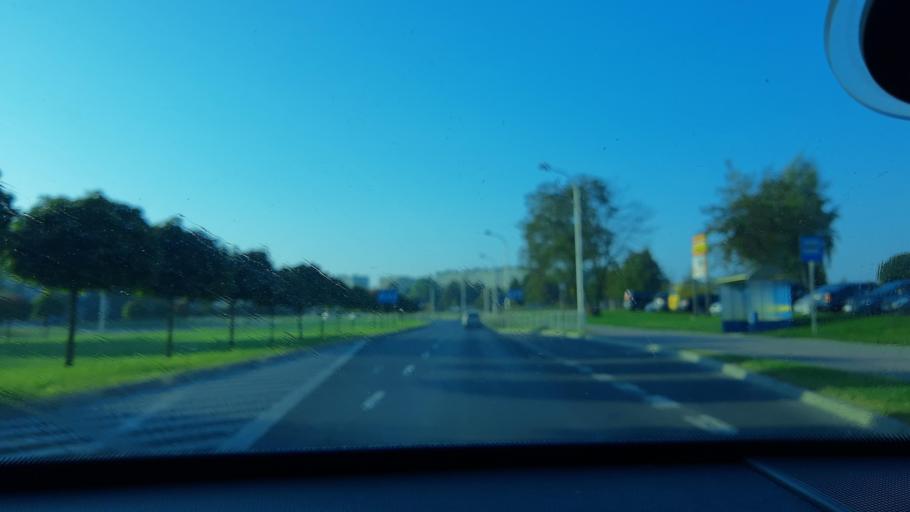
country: PL
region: Lodz Voivodeship
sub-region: Powiat sieradzki
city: Sieradz
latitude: 51.5927
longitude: 18.7146
